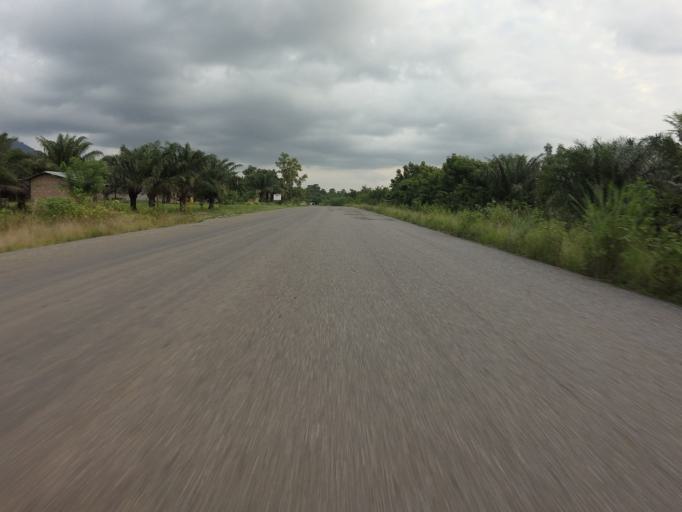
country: GH
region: Volta
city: Kpandu
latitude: 6.8207
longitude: 0.3765
